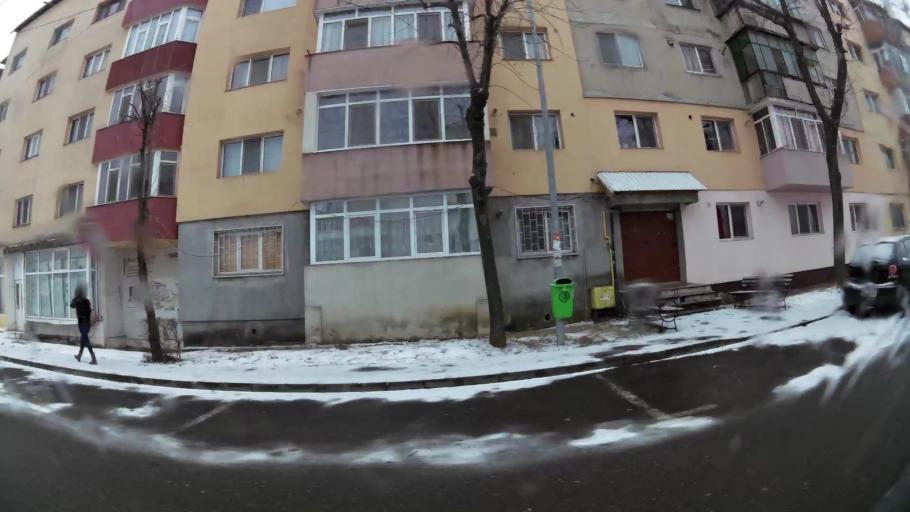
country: RO
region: Dambovita
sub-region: Municipiul Targoviste
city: Targoviste
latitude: 44.9154
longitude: 25.4785
